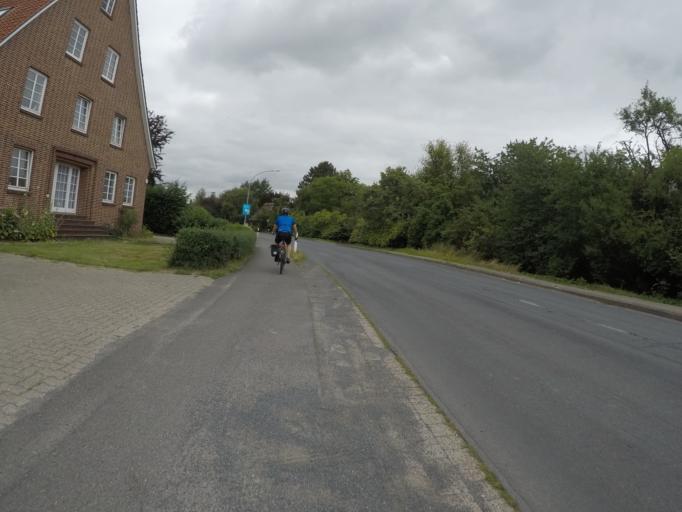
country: DE
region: Lower Saxony
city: Grunendeich
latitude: 53.5780
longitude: 9.6037
